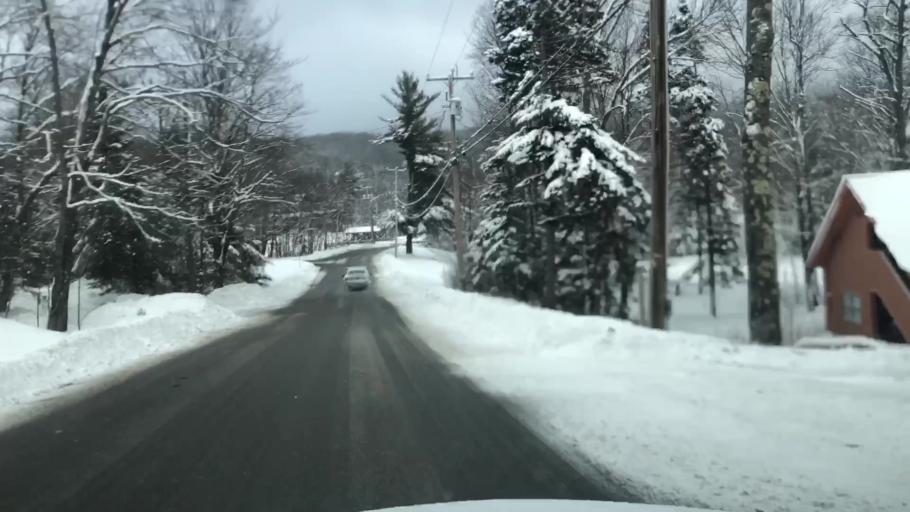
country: US
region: Vermont
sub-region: Rutland County
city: Rutland
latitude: 43.6464
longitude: -72.7872
